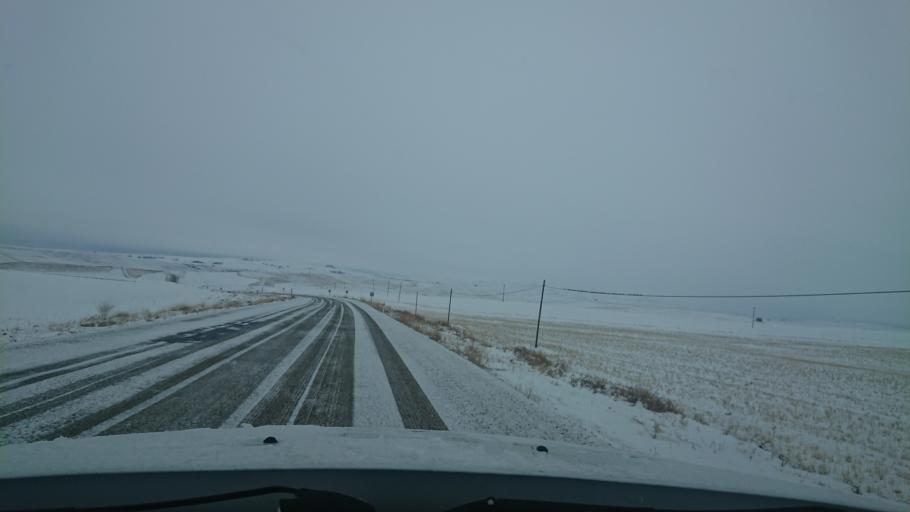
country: TR
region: Aksaray
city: Agacoren
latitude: 38.7802
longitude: 33.8718
